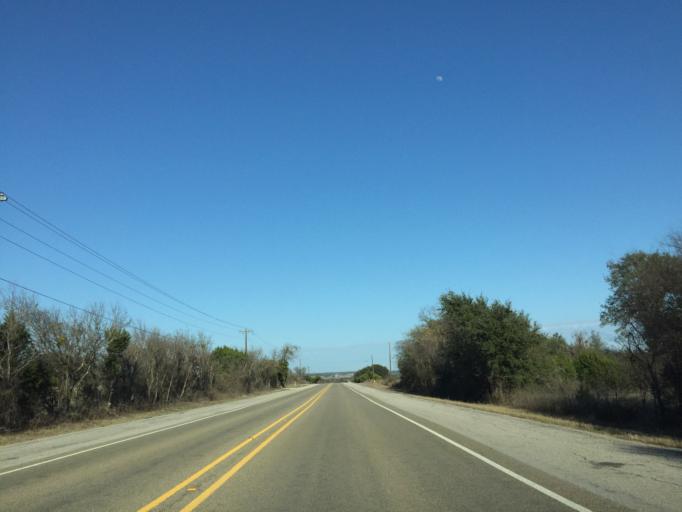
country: US
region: Texas
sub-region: Williamson County
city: Florence
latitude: 30.7698
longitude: -97.8265
